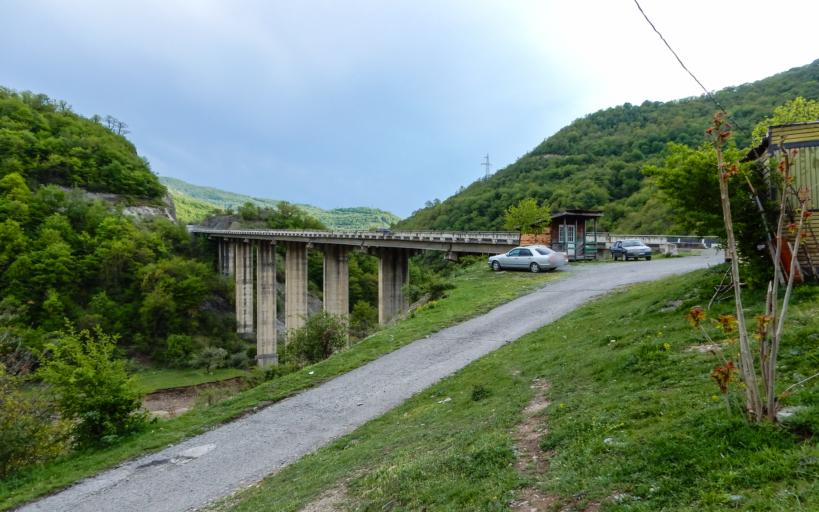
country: GE
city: Zhinvali
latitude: 42.1637
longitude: 44.7024
